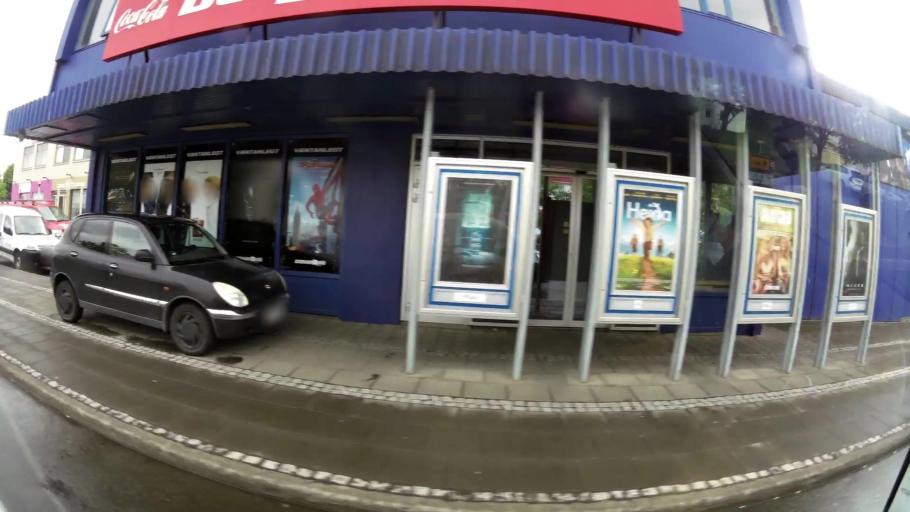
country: IS
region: Northeast
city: Akureyri
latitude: 65.6839
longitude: -18.0926
